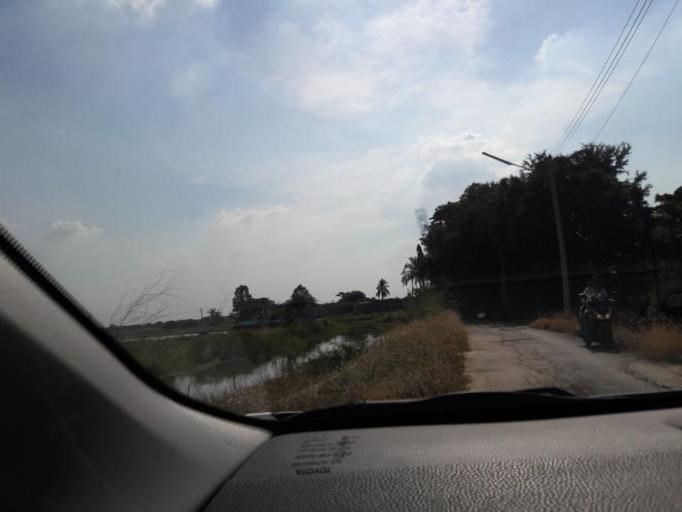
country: TH
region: Ang Thong
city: Wiset Chaichan
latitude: 14.5593
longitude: 100.3922
